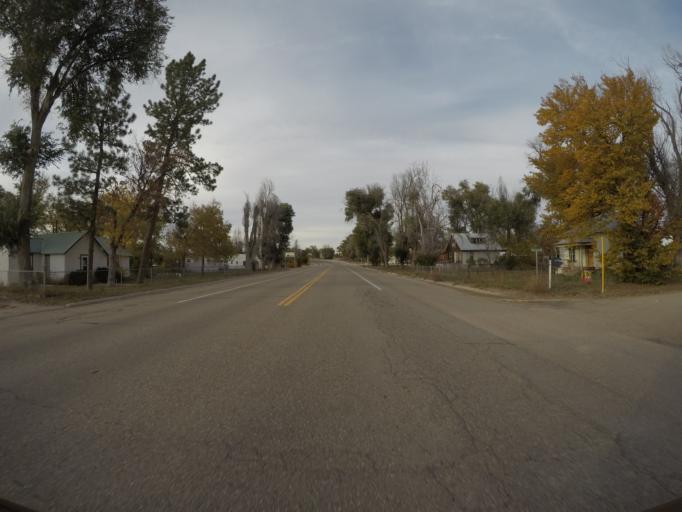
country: US
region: Colorado
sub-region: Yuma County
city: Yuma
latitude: 39.6658
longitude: -102.8508
